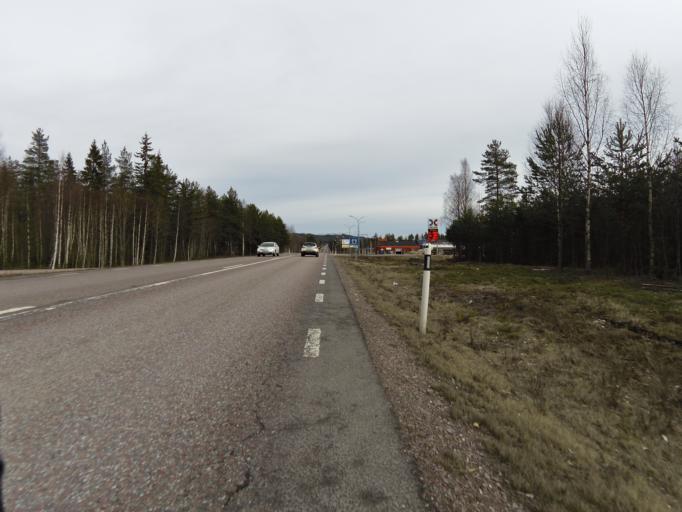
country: SE
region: Gaevleborg
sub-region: Hofors Kommun
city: Hofors
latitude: 60.5416
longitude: 16.2618
